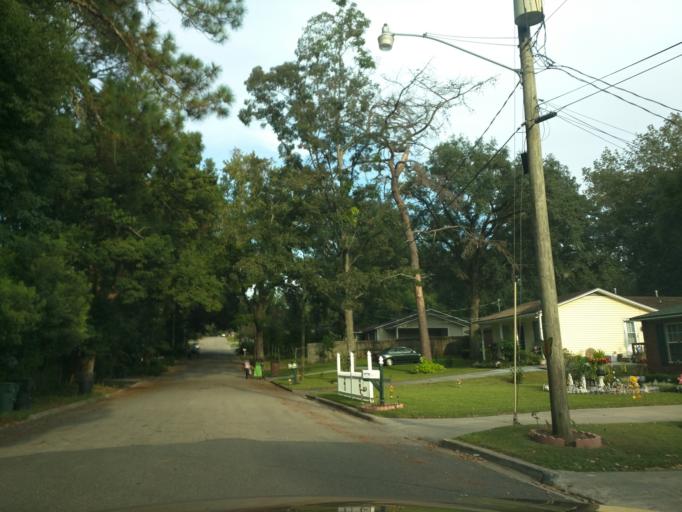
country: US
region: Florida
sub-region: Leon County
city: Tallahassee
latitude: 30.4557
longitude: -84.2896
